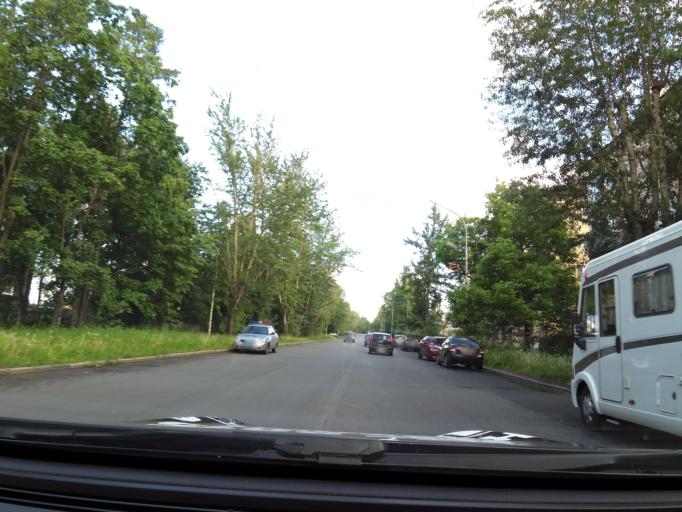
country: RU
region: Republic of Karelia
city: Petrozavodsk
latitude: 61.7849
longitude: 34.3963
